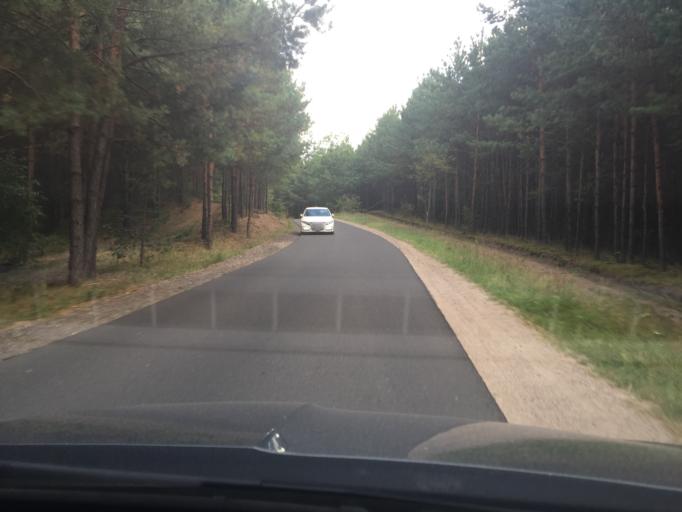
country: DE
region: Brandenburg
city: Grunheide
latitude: 52.3620
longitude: 13.7895
